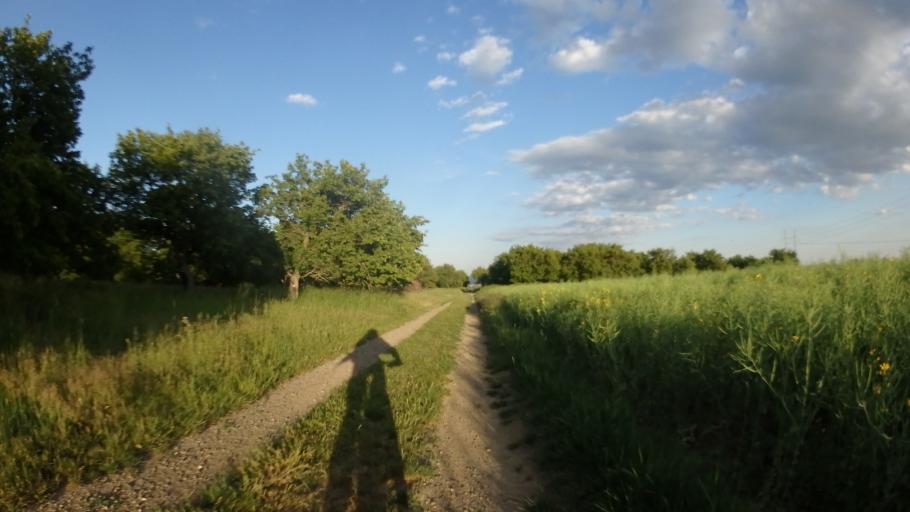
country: CZ
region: South Moravian
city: Zelesice
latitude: 49.1291
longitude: 16.5825
